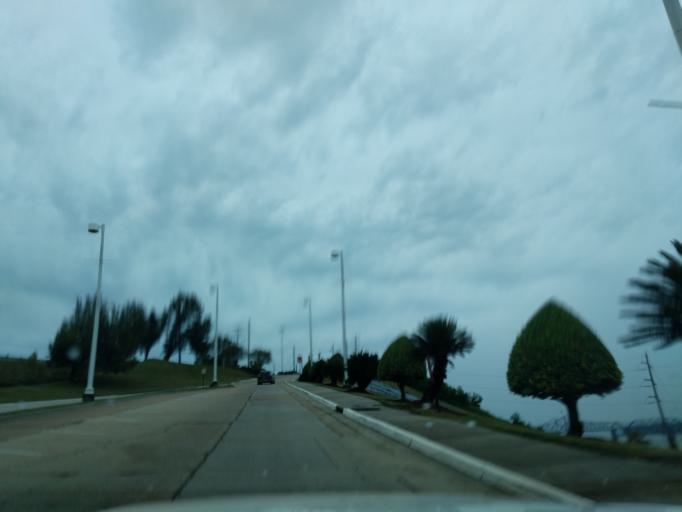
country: US
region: Mississippi
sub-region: Warren County
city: Vicksburg
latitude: 32.3241
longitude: -90.8954
